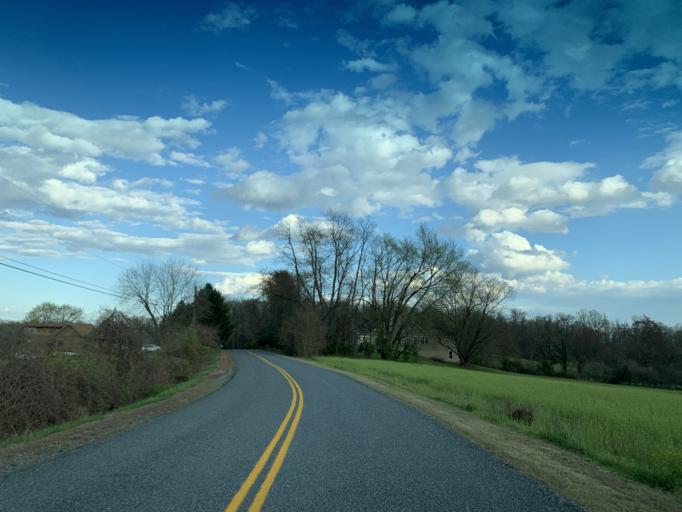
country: US
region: Maryland
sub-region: Harford County
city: South Bel Air
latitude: 39.5959
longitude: -76.3107
